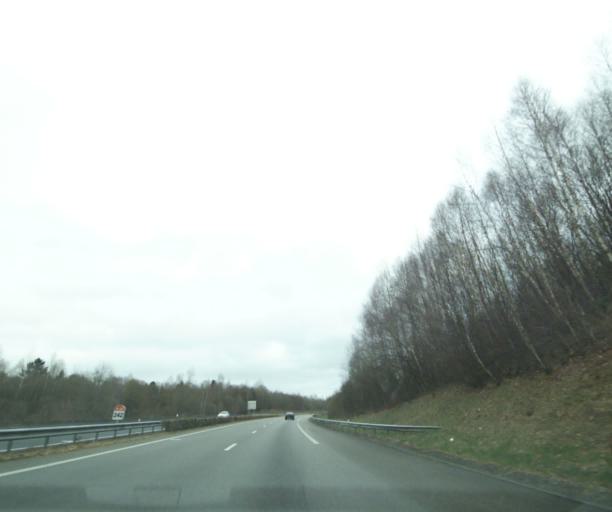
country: FR
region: Limousin
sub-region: Departement de la Correze
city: Uzerche
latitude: 45.4059
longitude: 1.5567
